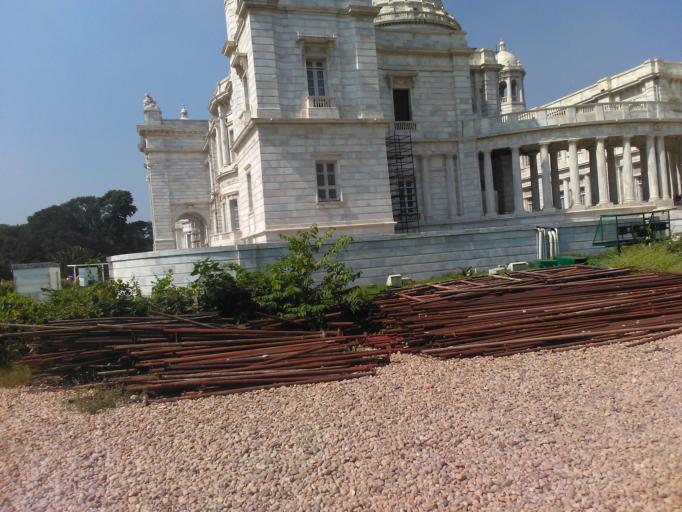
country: IN
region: West Bengal
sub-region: Kolkata
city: Bara Bazar
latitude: 22.5443
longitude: 88.3433
